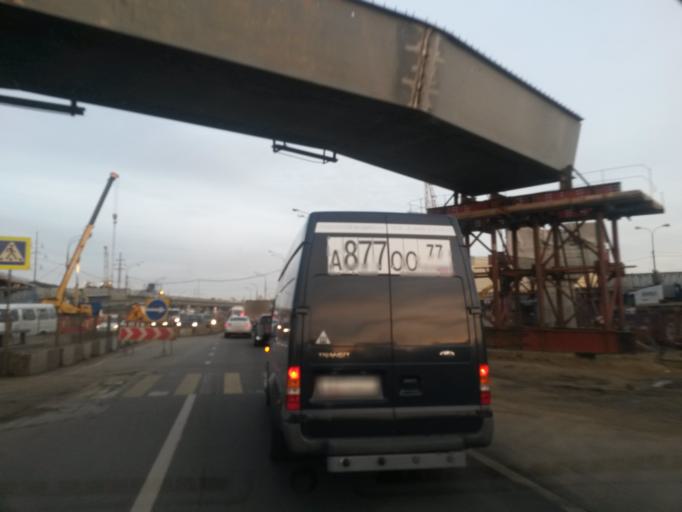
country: RU
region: Moskovskaya
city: Bol'shaya Setun'
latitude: 55.7001
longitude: 37.4218
